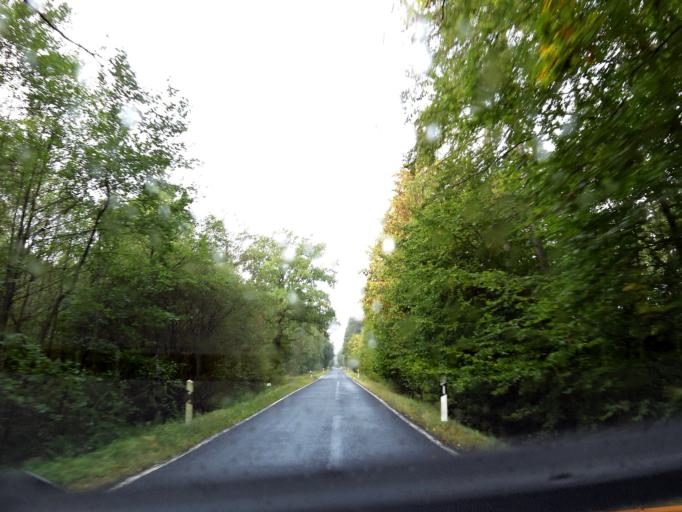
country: DE
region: Rheinland-Pfalz
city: Dorrebach
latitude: 49.9325
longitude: 7.7102
